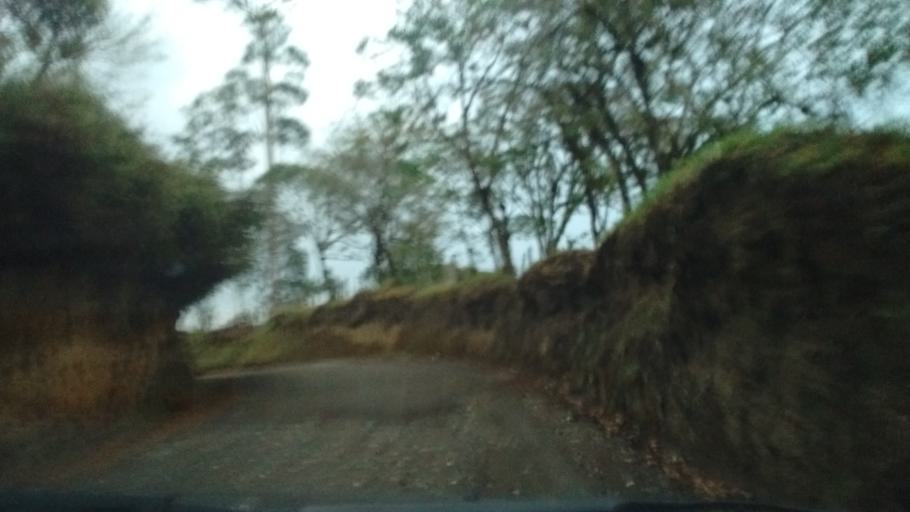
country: CO
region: Cauca
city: Lopez
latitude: 2.3827
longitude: -76.7237
